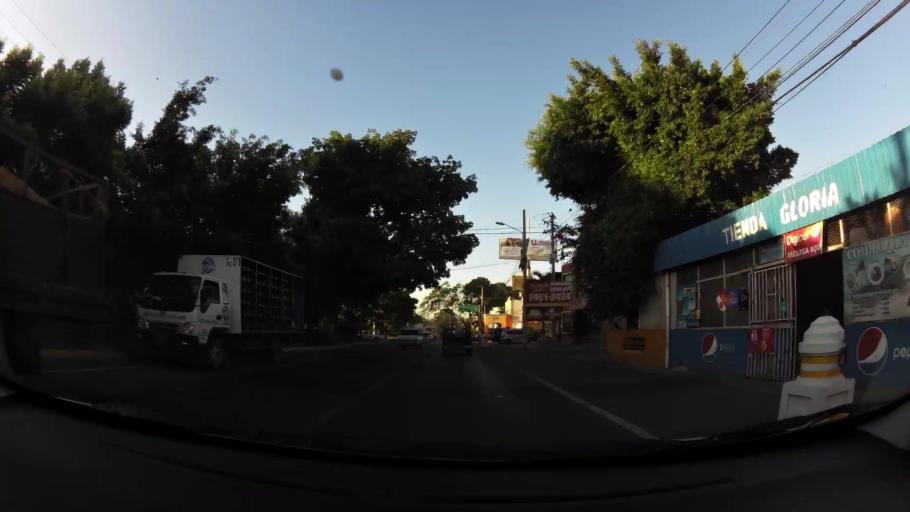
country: SV
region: Sonsonate
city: Sonsonate
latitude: 13.7111
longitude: -89.7278
